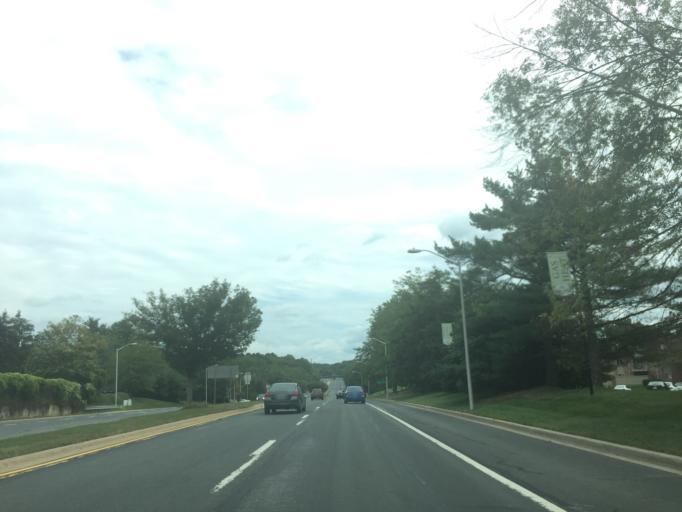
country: US
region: Maryland
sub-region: Montgomery County
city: Gaithersburg
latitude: 39.1597
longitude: -77.2006
